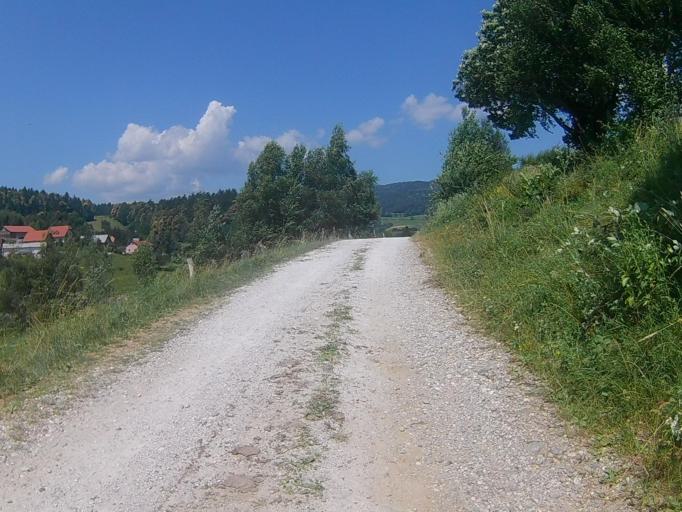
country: SI
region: Race-Fram
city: Fram
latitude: 46.4772
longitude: 15.6090
